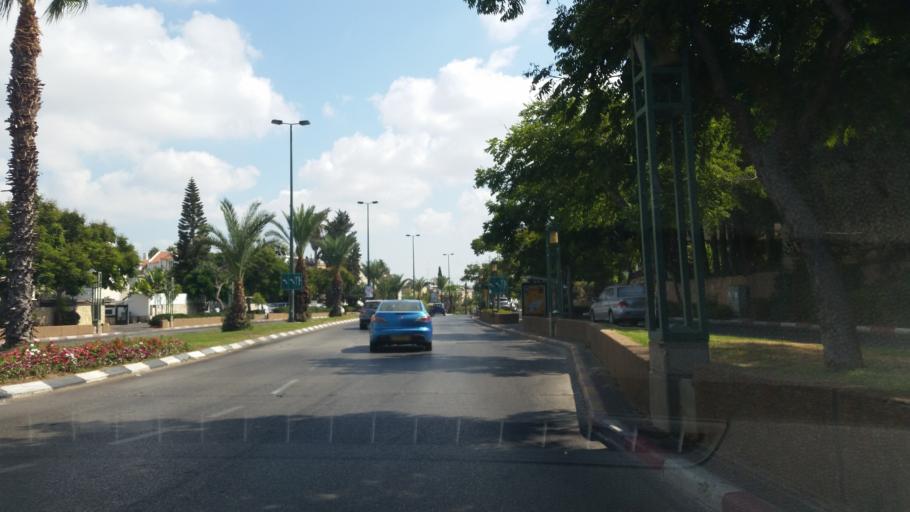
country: IL
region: Tel Aviv
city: Ramat HaSharon
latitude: 32.1219
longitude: 34.8248
